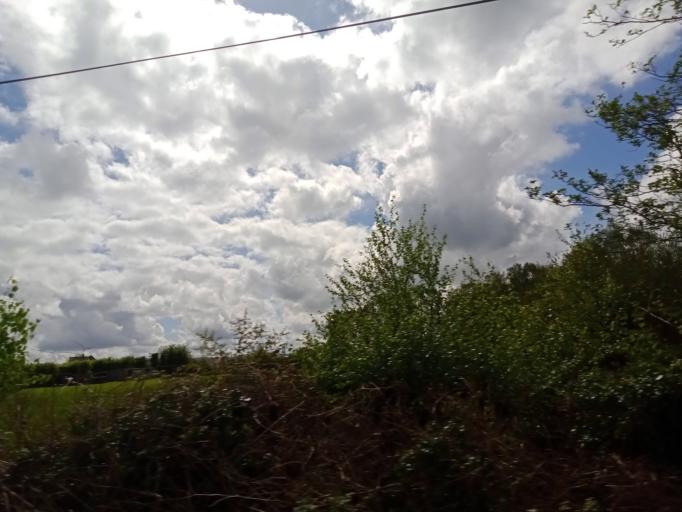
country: IE
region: Munster
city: Thurles
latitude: 52.6905
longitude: -7.6464
